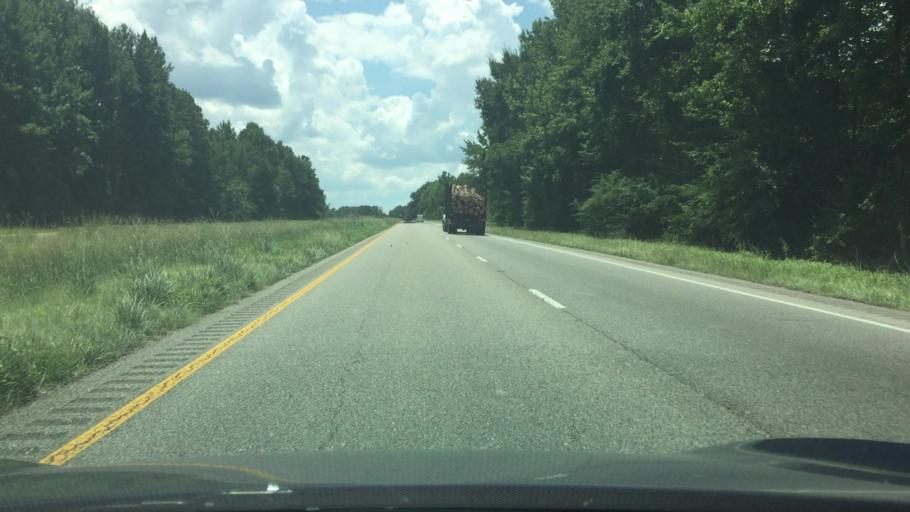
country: US
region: Alabama
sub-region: Montgomery County
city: Taylor
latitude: 32.0822
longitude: -86.0638
